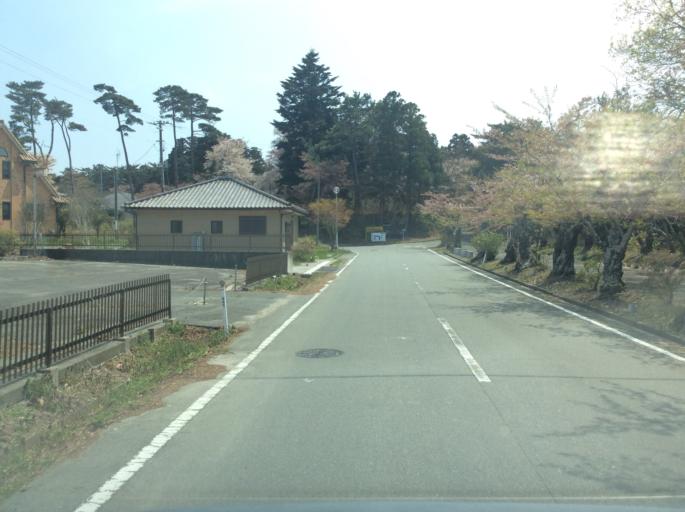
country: JP
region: Fukushima
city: Namie
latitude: 37.2690
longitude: 141.0107
